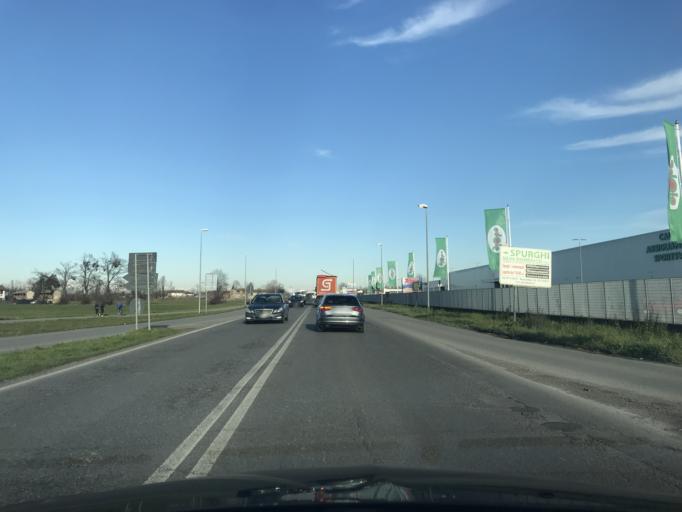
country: IT
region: Lombardy
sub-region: Provincia di Lodi
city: Muzza di Cornegliano Laudense
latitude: 45.2800
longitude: 9.4609
